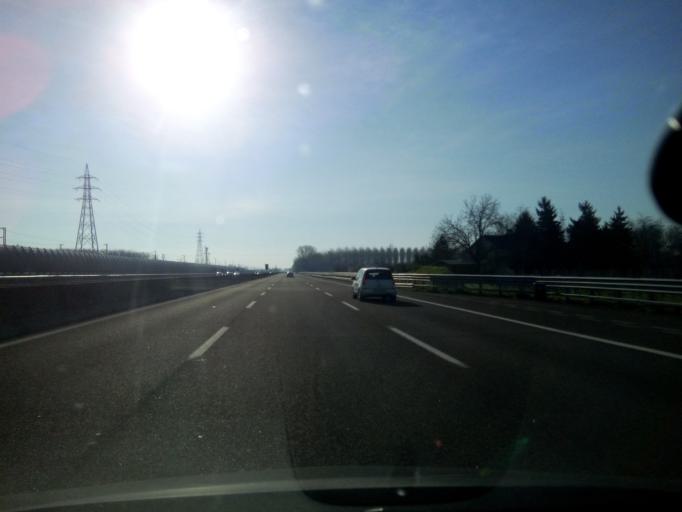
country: IT
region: Emilia-Romagna
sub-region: Provincia di Reggio Emilia
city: Rubiera
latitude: 44.6816
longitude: 10.8039
